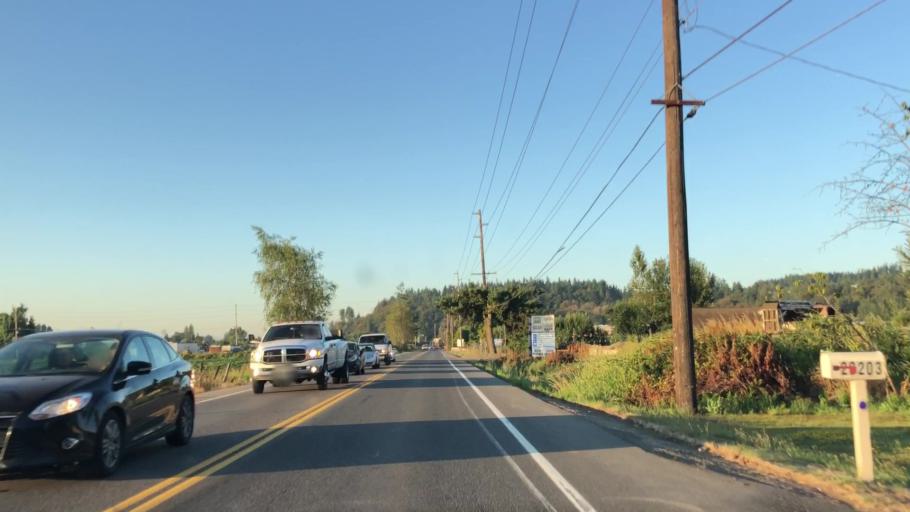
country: US
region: Washington
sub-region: King County
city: Lakeland North
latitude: 47.3490
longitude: -122.2497
